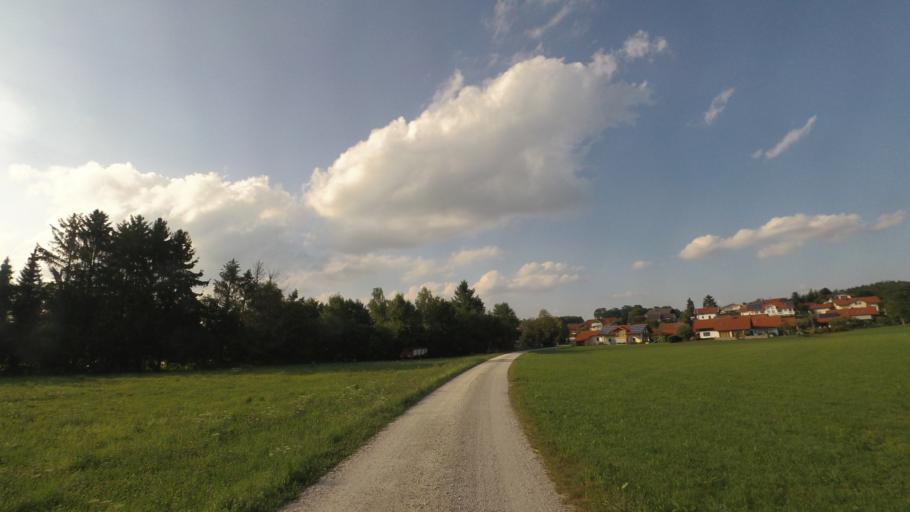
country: DE
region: Bavaria
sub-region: Upper Bavaria
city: Chieming
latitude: 47.9077
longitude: 12.5594
